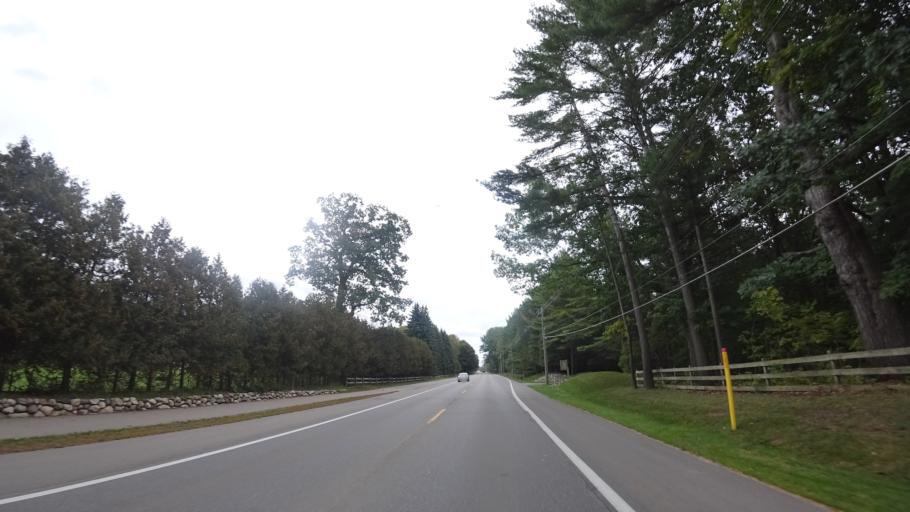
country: US
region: Michigan
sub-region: Emmet County
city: Harbor Springs
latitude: 45.4315
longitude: -84.9586
